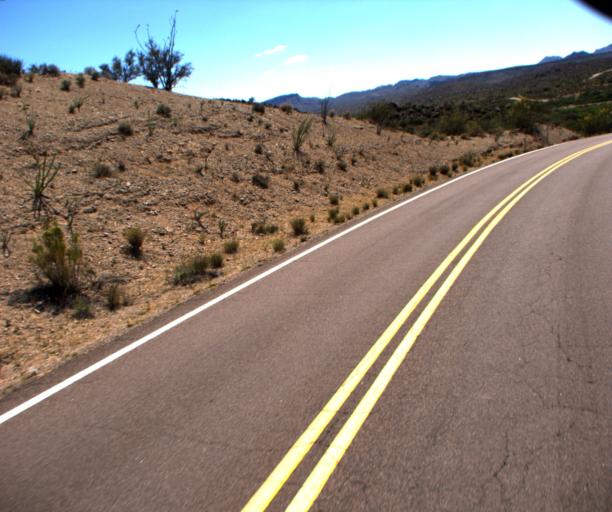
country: US
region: Arizona
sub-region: Yavapai County
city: Bagdad
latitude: 34.4661
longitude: -113.2234
